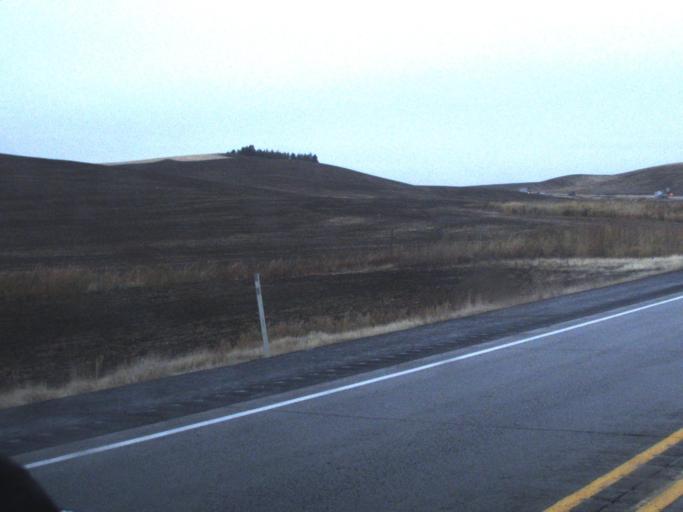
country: US
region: Washington
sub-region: Whitman County
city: Colfax
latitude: 46.9717
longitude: -117.3229
